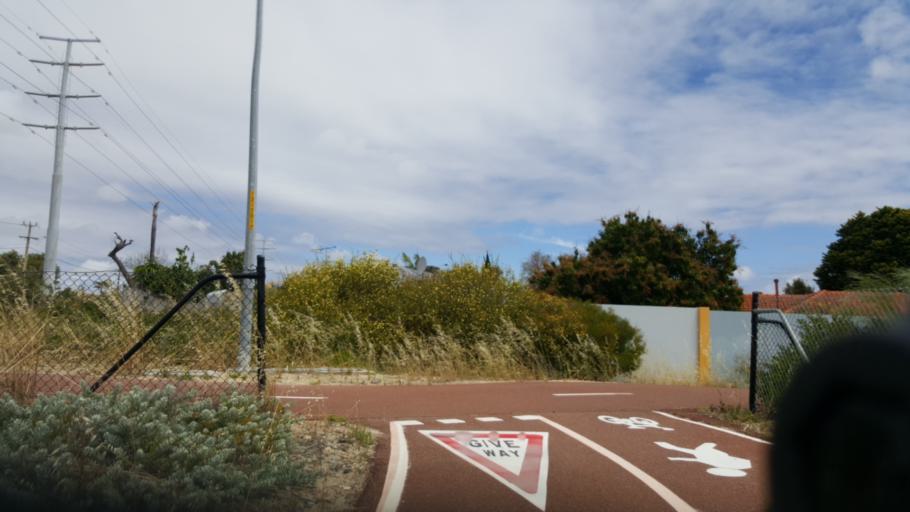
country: AU
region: Western Australia
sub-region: Bayswater
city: Embleton
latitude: -31.8686
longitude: 115.8884
